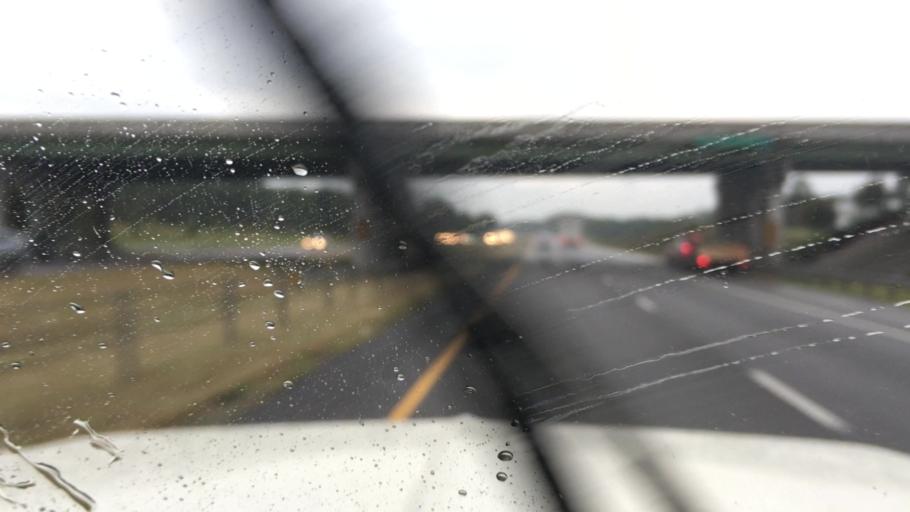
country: US
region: Alabama
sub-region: Morgan County
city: Falkville
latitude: 34.4128
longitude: -86.8985
